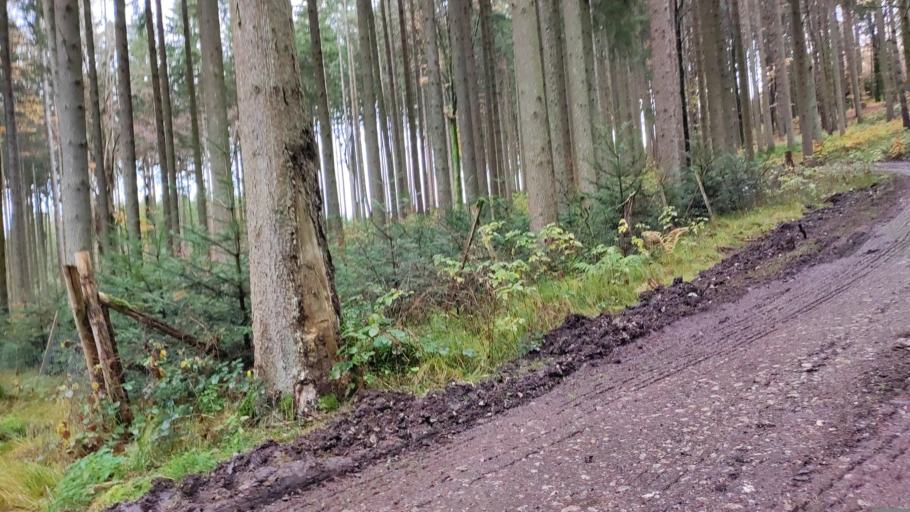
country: DE
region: Bavaria
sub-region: Swabia
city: Dinkelscherben
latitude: 48.3557
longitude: 10.5332
